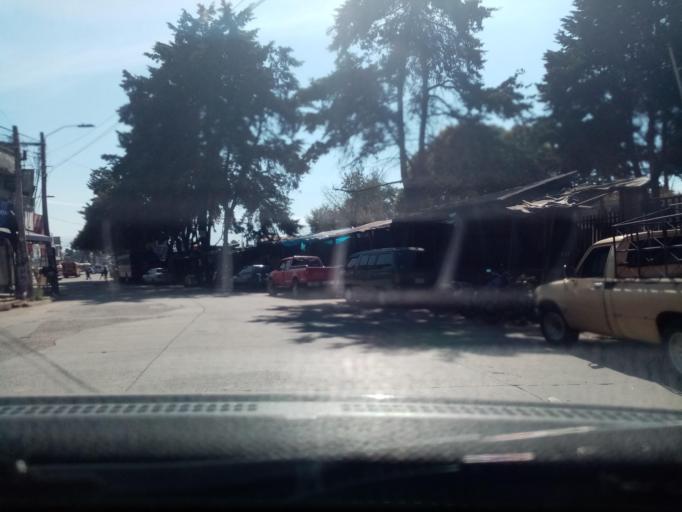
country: GT
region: Quetzaltenango
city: Quetzaltenango
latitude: 14.8488
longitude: -91.5334
